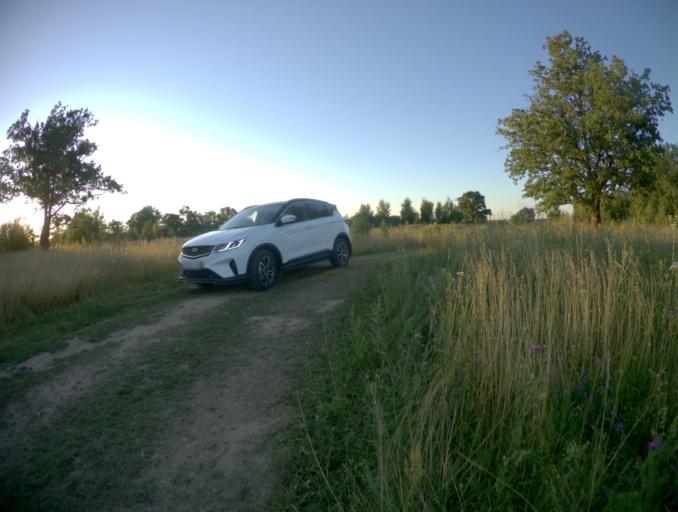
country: RU
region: Vladimir
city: Galitsy
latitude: 56.1790
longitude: 42.8066
